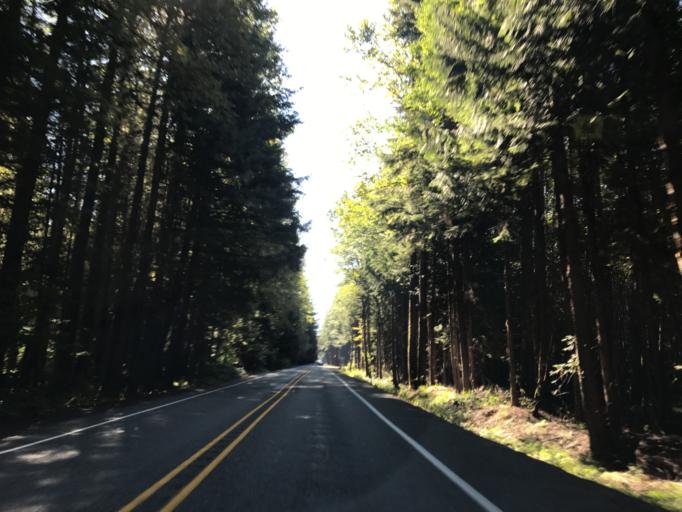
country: US
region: Washington
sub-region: King County
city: Riverbend
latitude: 47.1201
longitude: -121.6113
